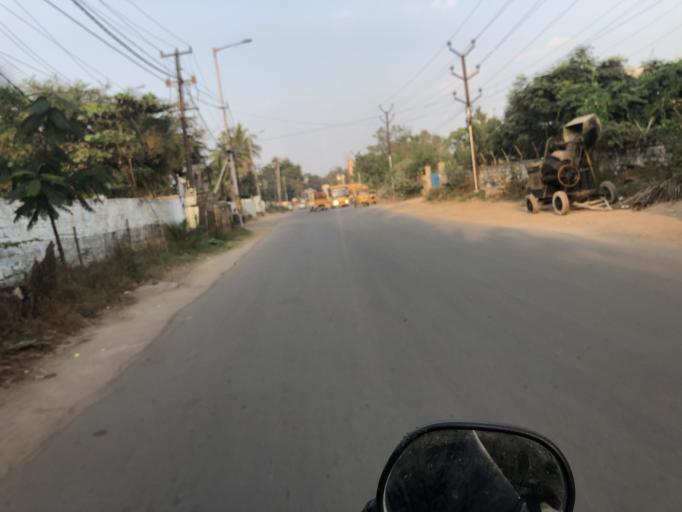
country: IN
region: Telangana
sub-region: Rangareddi
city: Kukatpalli
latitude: 17.4627
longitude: 78.4409
